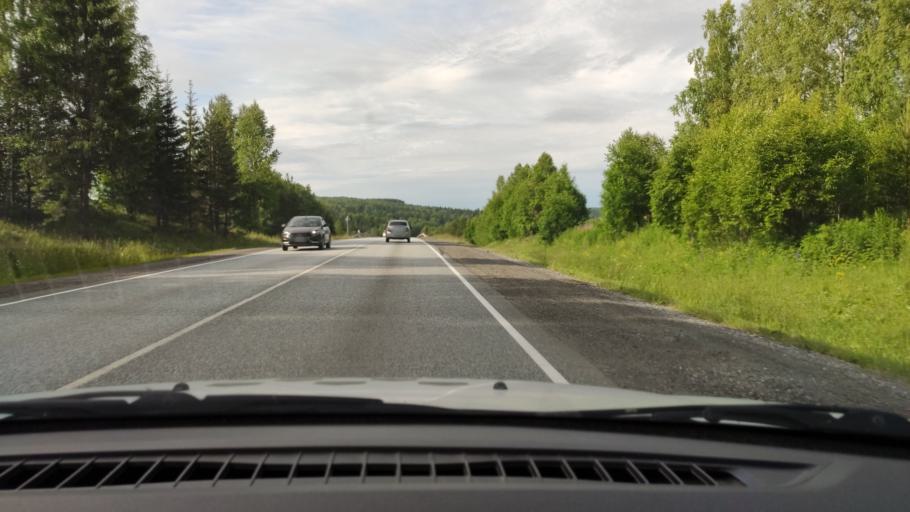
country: RU
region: Perm
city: Pavlovskiy
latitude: 57.9043
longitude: 54.9541
